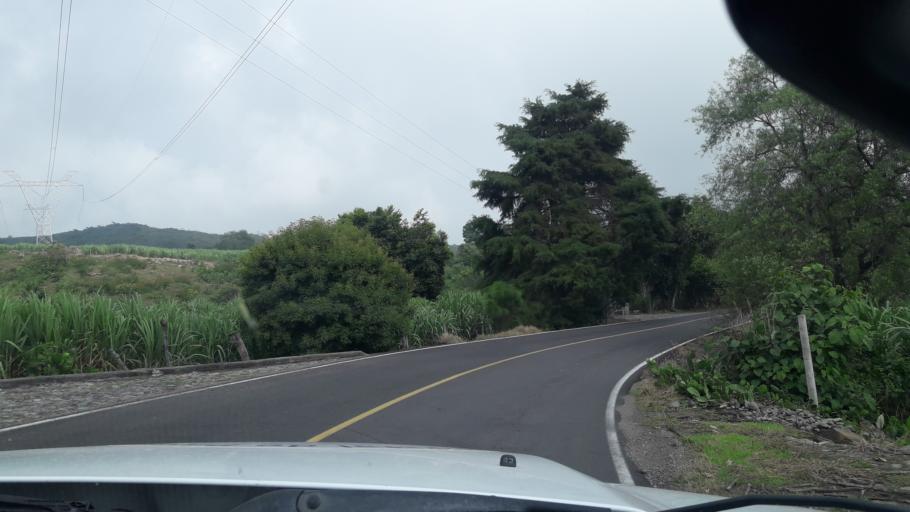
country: MX
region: Colima
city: Queseria
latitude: 19.4095
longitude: -103.6394
